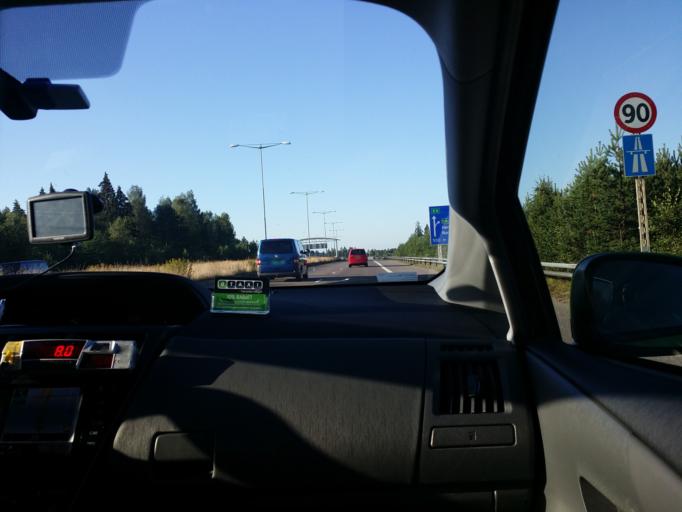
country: NO
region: Akershus
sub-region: Nannestad
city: Teigebyen
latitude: 60.1874
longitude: 11.0947
